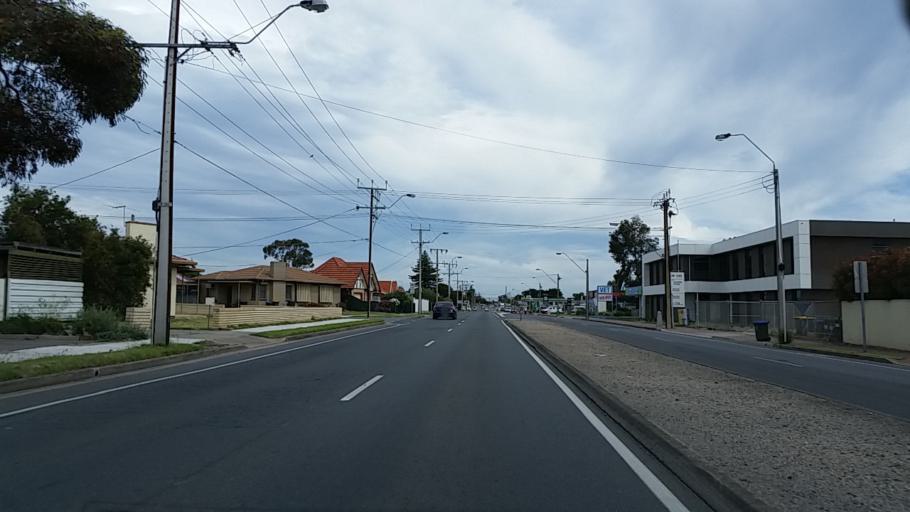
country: AU
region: South Australia
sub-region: Charles Sturt
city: Seaton
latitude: -34.8993
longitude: 138.5143
